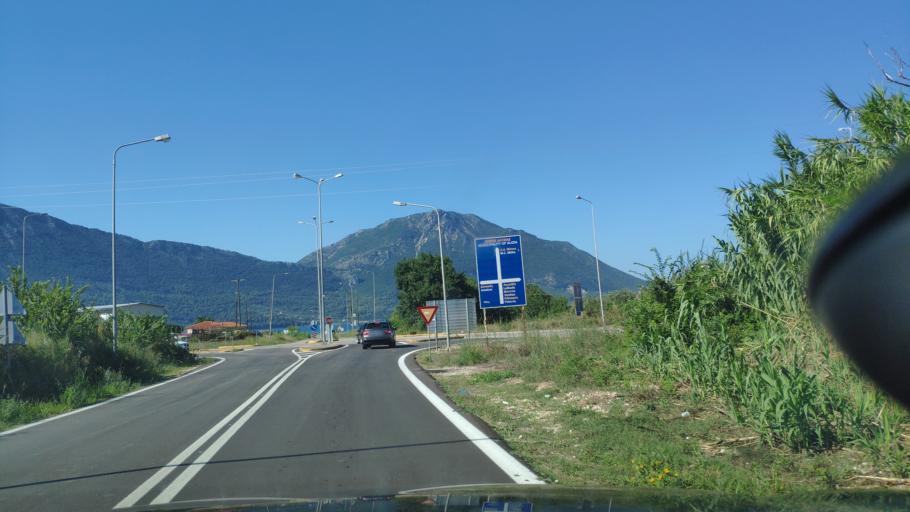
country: GR
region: West Greece
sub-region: Nomos Aitolias kai Akarnanias
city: Kandila
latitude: 38.6767
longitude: 20.9404
